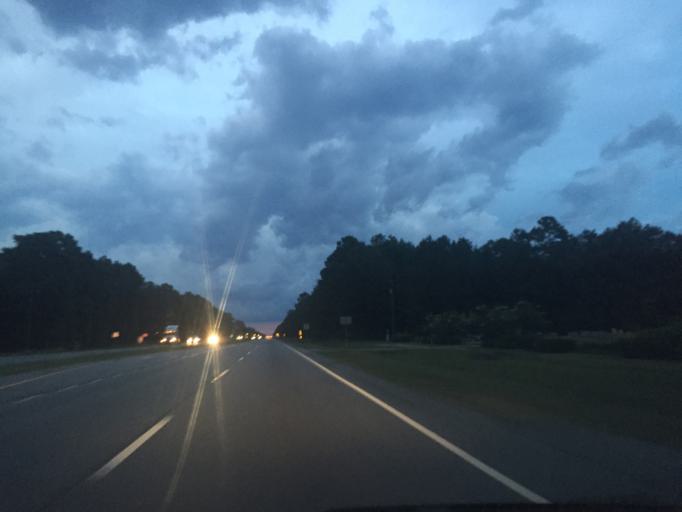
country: US
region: Georgia
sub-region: Bryan County
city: Richmond Hill
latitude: 31.8928
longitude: -81.3788
